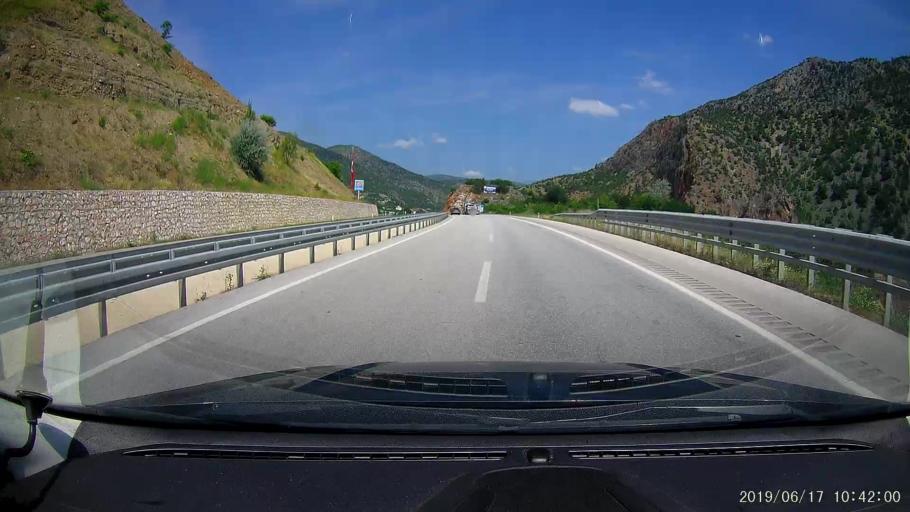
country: TR
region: Corum
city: Kargi
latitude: 41.0454
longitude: 34.5634
